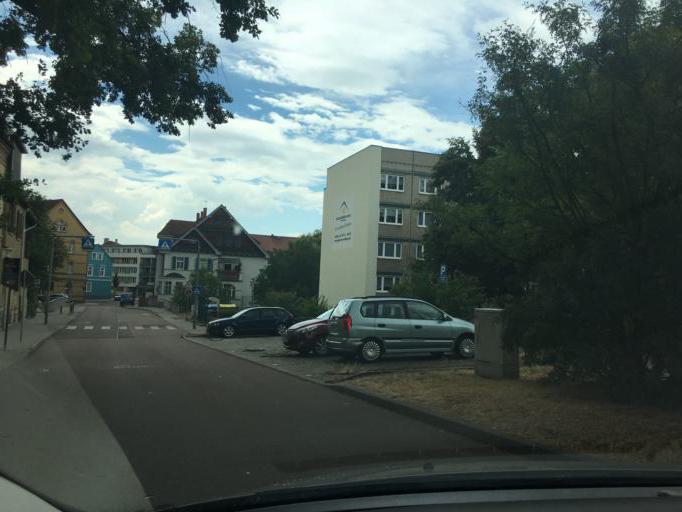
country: DE
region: Saxony-Anhalt
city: Merseburg
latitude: 51.3590
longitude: 11.9979
